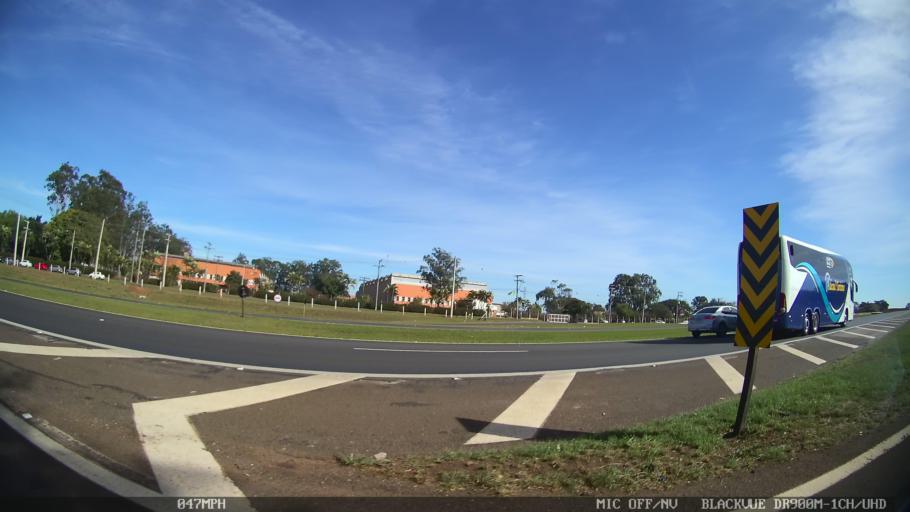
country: BR
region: Sao Paulo
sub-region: Leme
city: Leme
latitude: -22.2048
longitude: -47.3948
